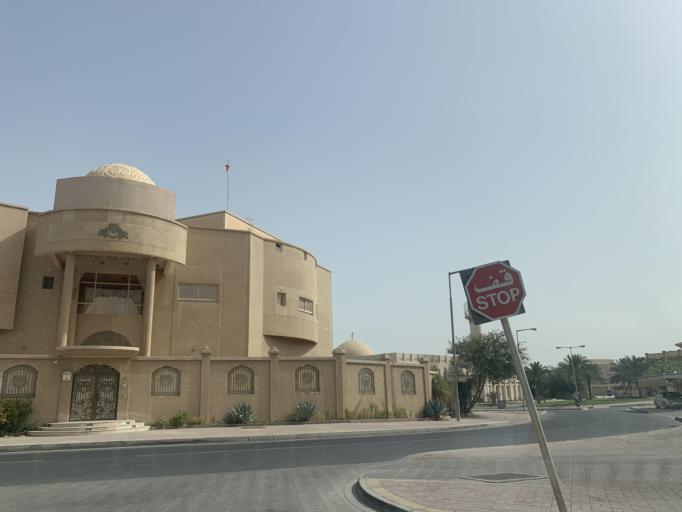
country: BH
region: Central Governorate
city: Madinat Hamad
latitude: 26.1410
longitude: 50.5142
